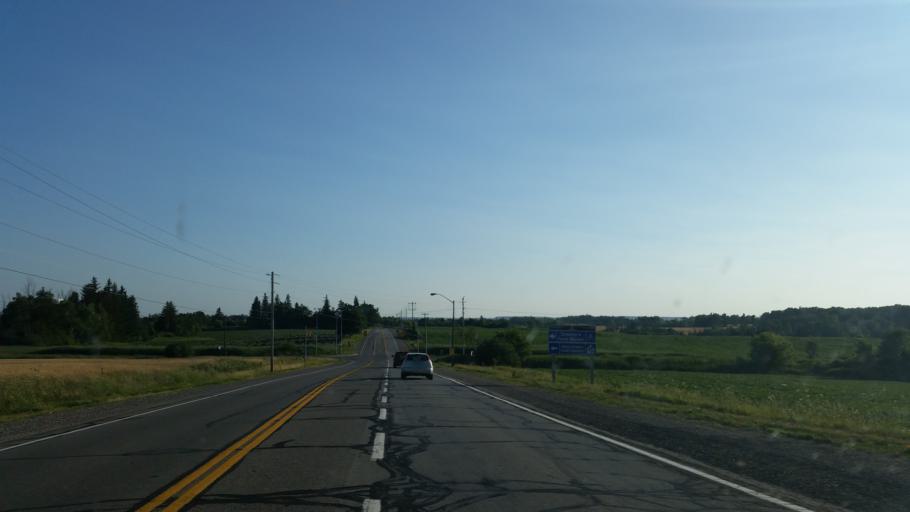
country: CA
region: Ontario
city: Brampton
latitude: 43.7937
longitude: -79.8555
